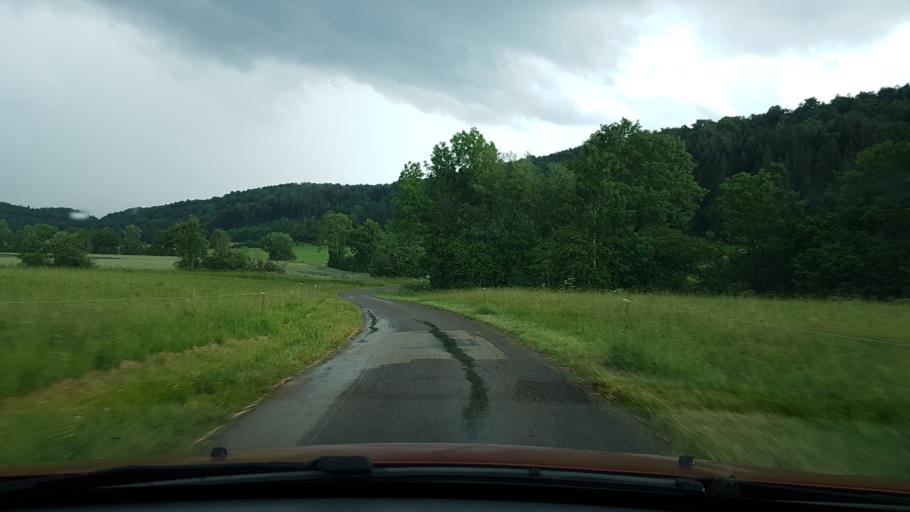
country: FR
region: Franche-Comte
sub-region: Departement du Jura
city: Clairvaux-les-Lacs
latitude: 46.5458
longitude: 5.7023
